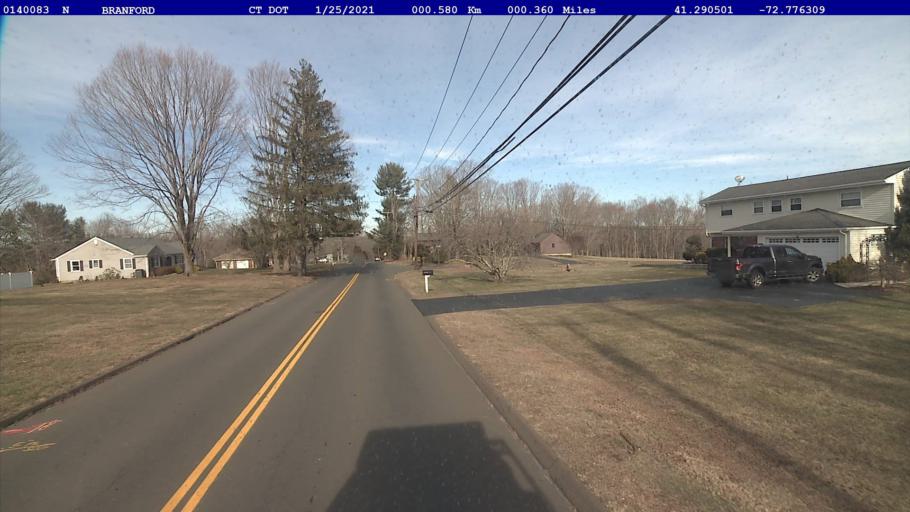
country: US
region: Connecticut
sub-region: New Haven County
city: North Branford
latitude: 41.2905
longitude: -72.7763
